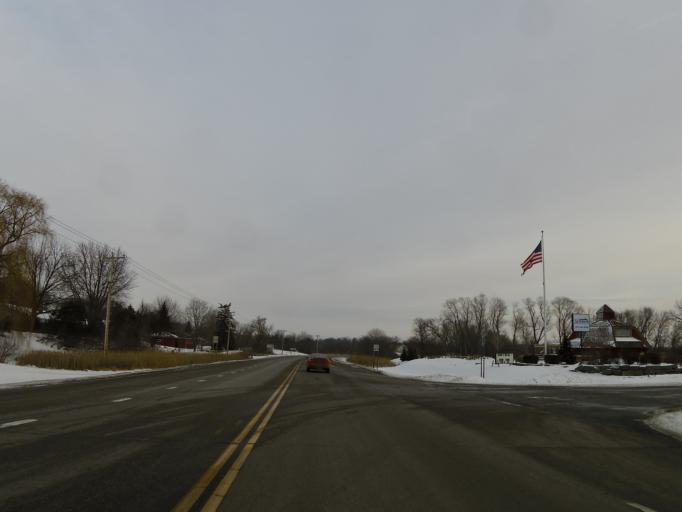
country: US
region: Minnesota
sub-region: Hennepin County
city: Saint Bonifacius
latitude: 44.9017
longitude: -93.7394
